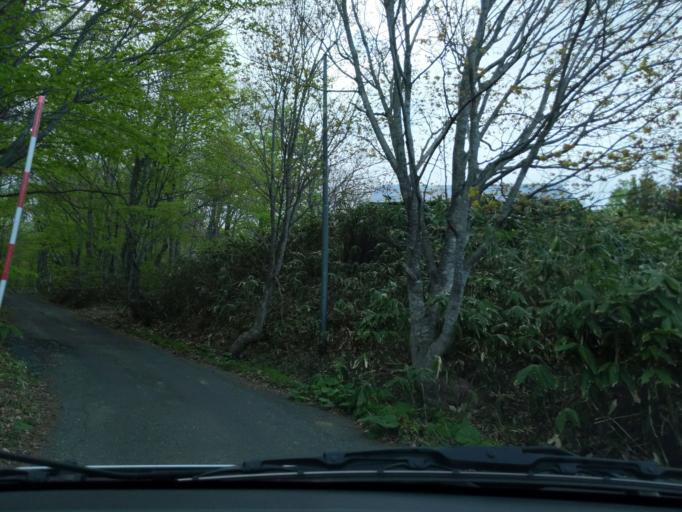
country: JP
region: Iwate
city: Ichinoseki
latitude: 38.9256
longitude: 140.8251
